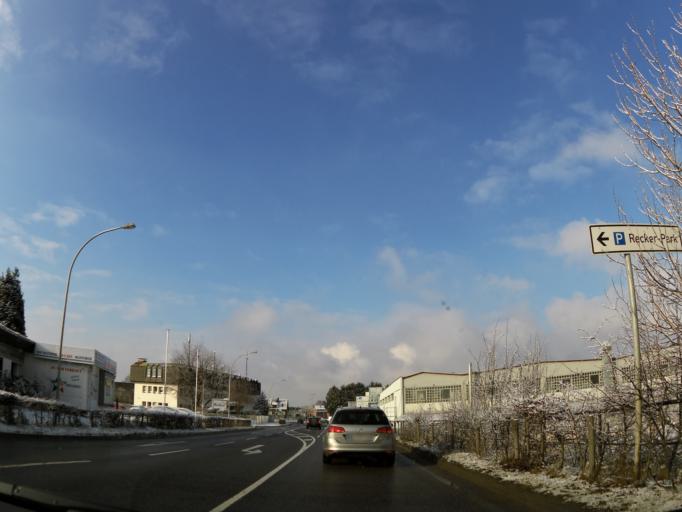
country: DE
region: North Rhine-Westphalia
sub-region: Regierungsbezirk Koln
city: Wurselen
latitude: 50.8312
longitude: 6.1328
